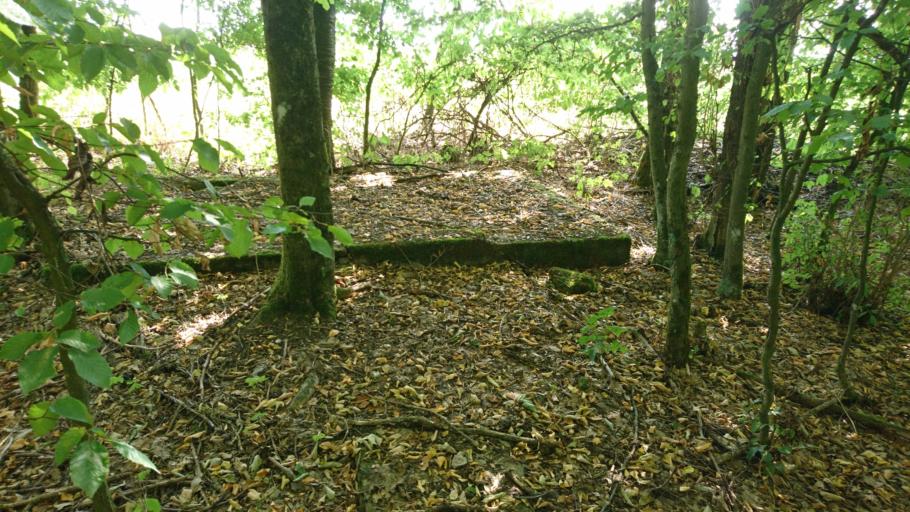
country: DE
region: Bavaria
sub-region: Regierungsbezirk Unterfranken
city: Kolitzheim
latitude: 49.9132
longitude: 10.2543
